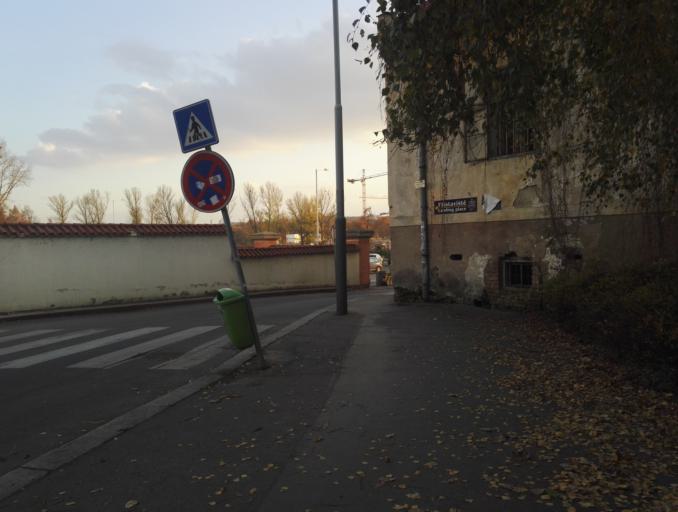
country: CZ
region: Praha
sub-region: Praha 1
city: Mala Strana
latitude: 50.1151
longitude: 14.4111
